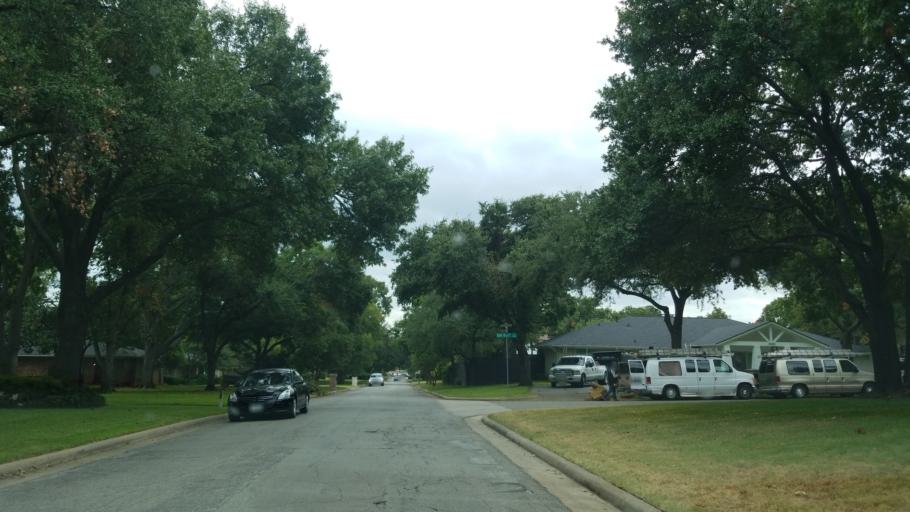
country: US
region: Texas
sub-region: Dallas County
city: Richardson
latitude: 32.9434
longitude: -96.7731
